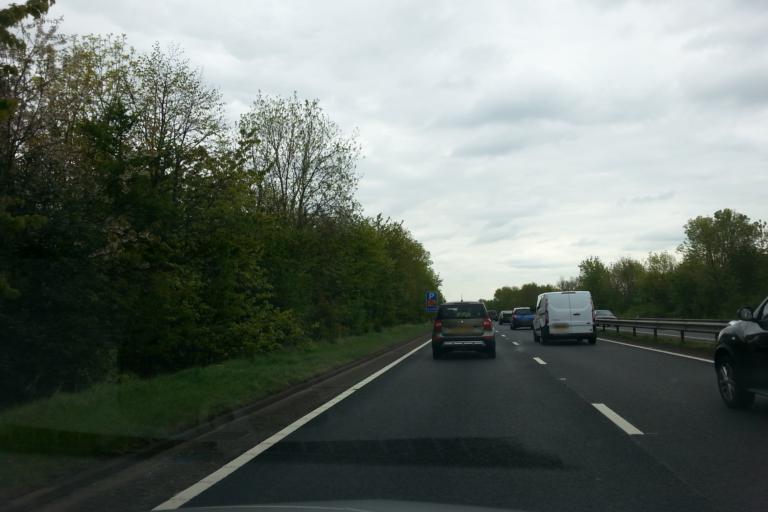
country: GB
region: England
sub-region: Leicestershire
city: Castle Donington
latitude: 52.7980
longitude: -1.3585
